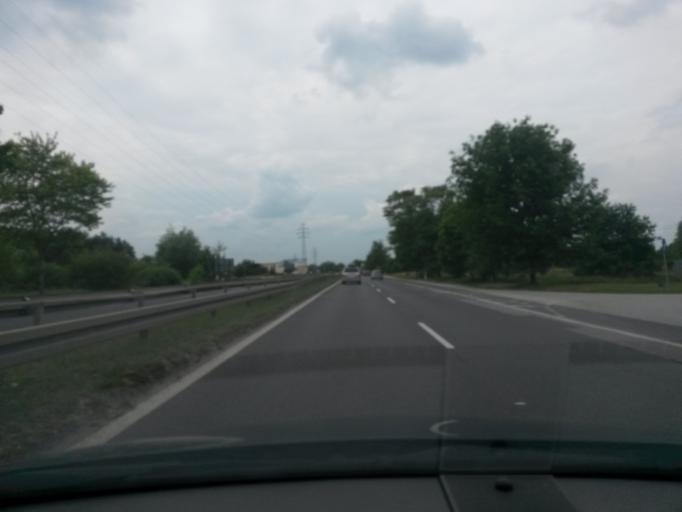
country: PL
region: Masovian Voivodeship
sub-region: Powiat pruszkowski
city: Nadarzyn
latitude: 52.1007
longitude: 20.8236
